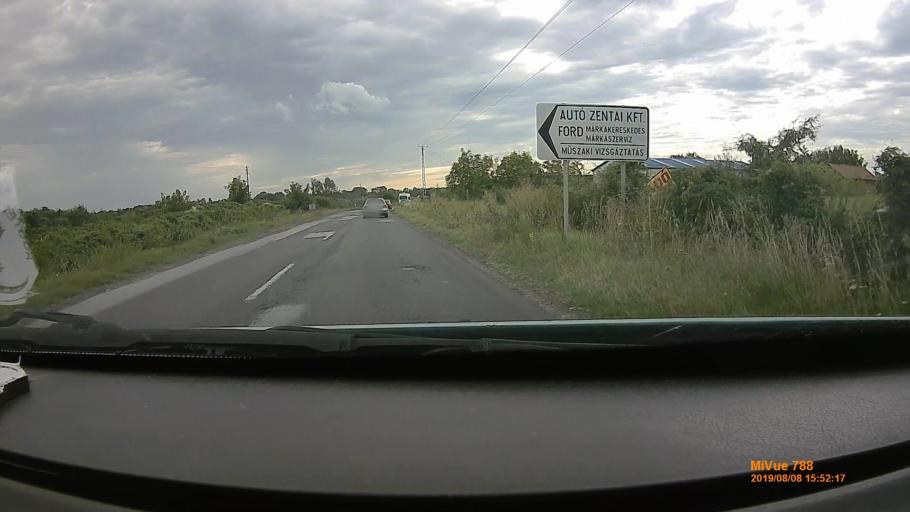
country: HU
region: Szabolcs-Szatmar-Bereg
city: Mateszalka
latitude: 47.9397
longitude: 22.3357
